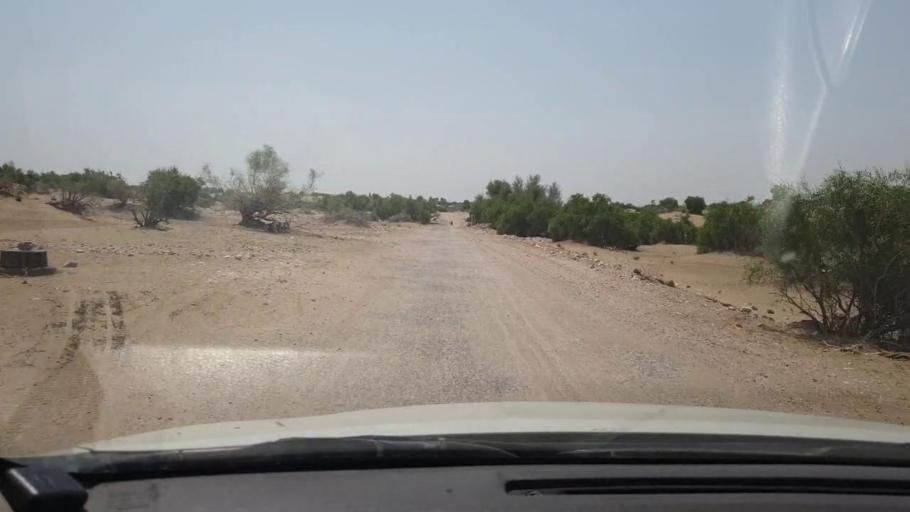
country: PK
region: Sindh
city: Rohri
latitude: 27.3181
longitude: 69.2789
